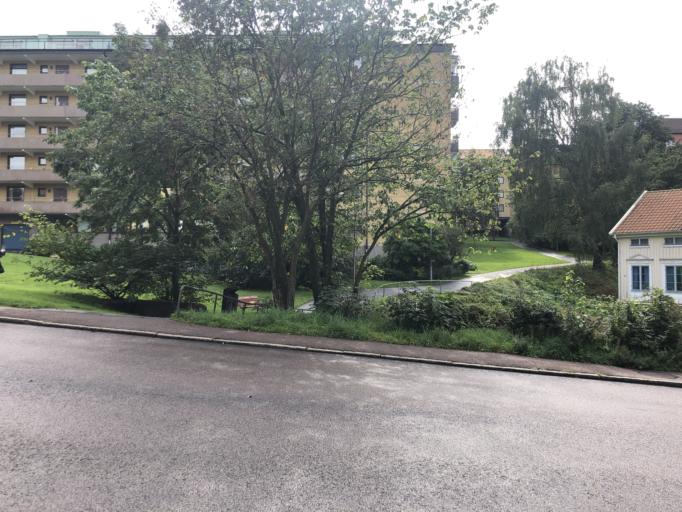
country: SE
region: Vaestra Goetaland
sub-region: Goteborg
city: Majorna
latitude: 57.6937
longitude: 11.9210
